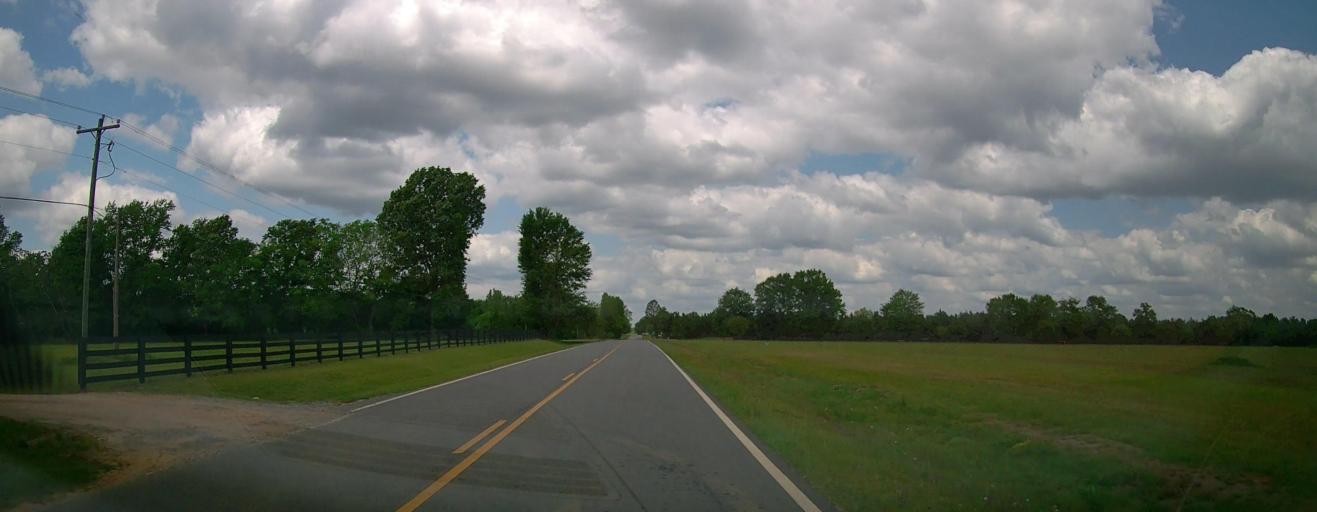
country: US
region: Georgia
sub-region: Laurens County
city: Dublin
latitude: 32.6034
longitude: -82.9592
